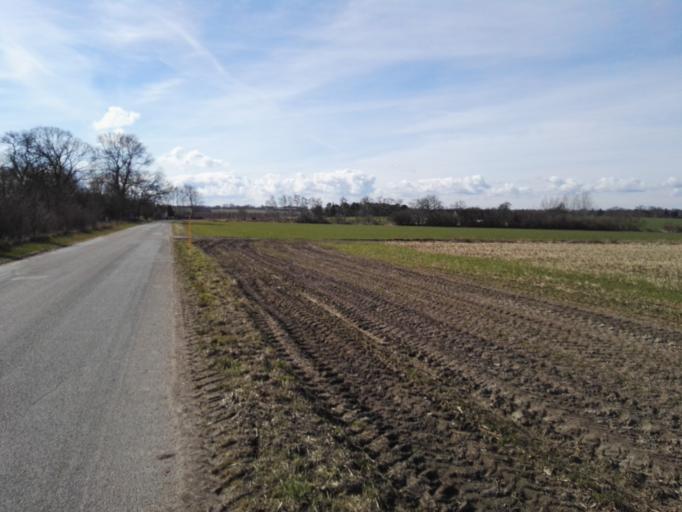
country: DK
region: Zealand
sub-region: Lejre Kommune
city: Ejby
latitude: 55.7821
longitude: 11.8315
